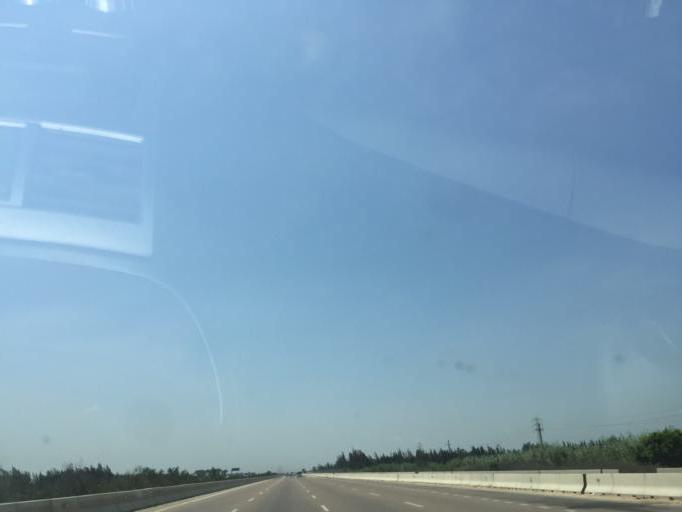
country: EG
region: Al Buhayrah
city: Abu al Matamir
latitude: 30.7424
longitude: 30.0051
